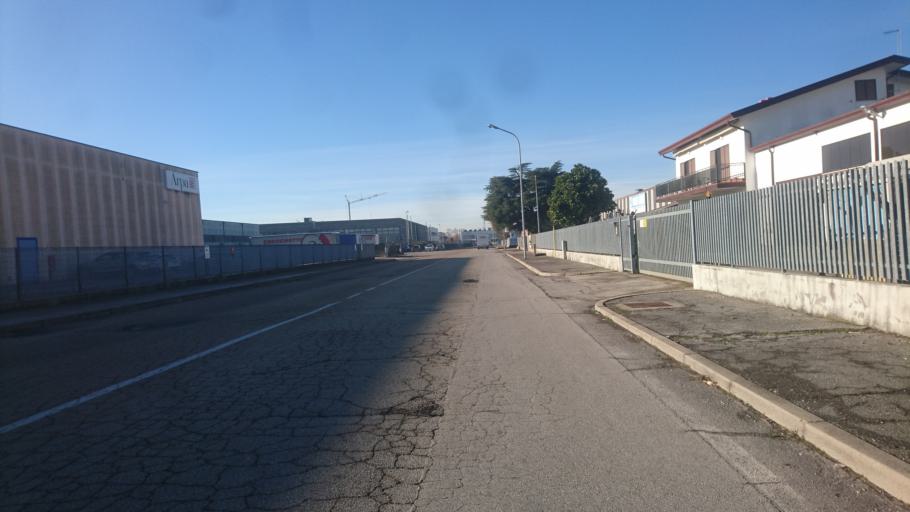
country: IT
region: Veneto
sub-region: Provincia di Padova
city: Limena
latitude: 45.4656
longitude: 11.8476
